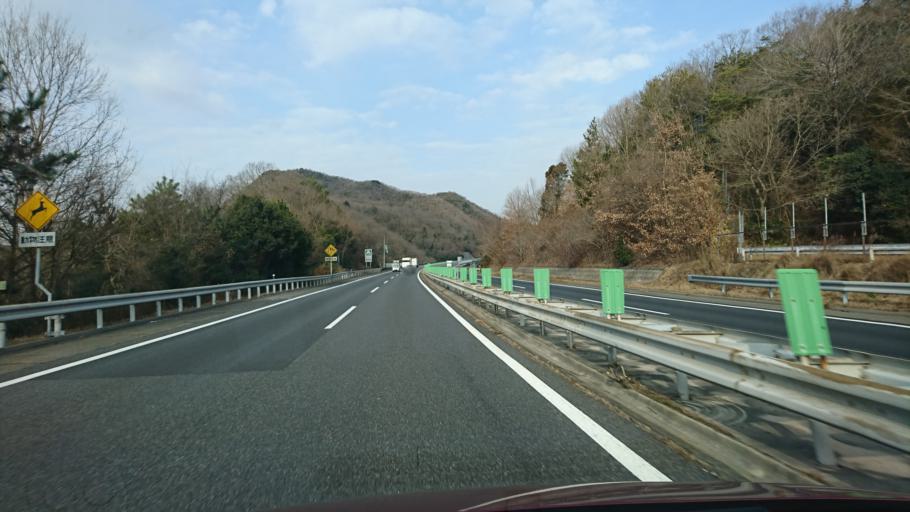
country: JP
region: Hyogo
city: Kariya
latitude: 34.7829
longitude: 134.2212
